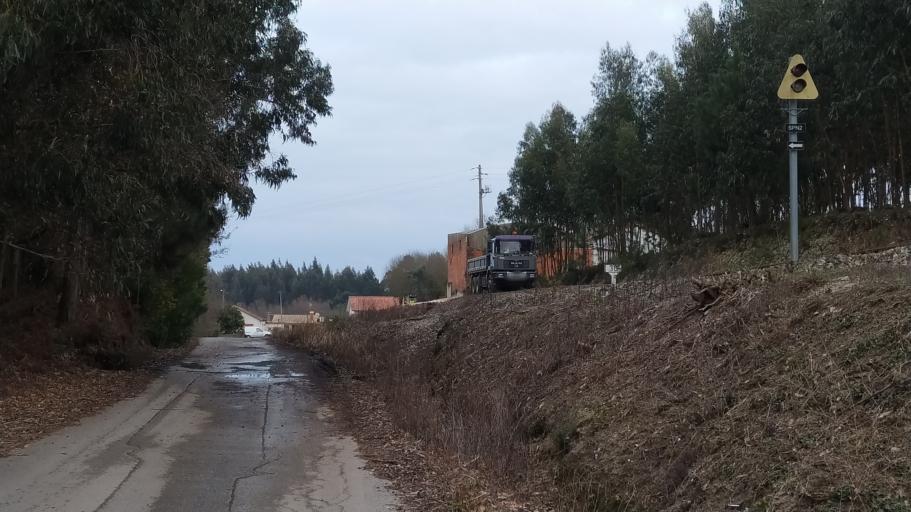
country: PT
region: Aveiro
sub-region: Aveiro
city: Eixo
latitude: 40.6397
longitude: -8.5902
